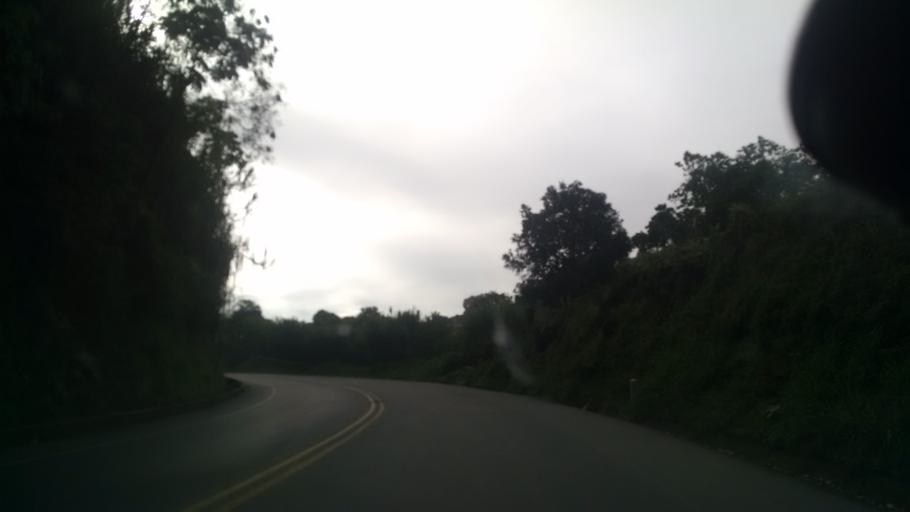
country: CO
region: Risaralda
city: Pereira
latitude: 4.8202
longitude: -75.7363
